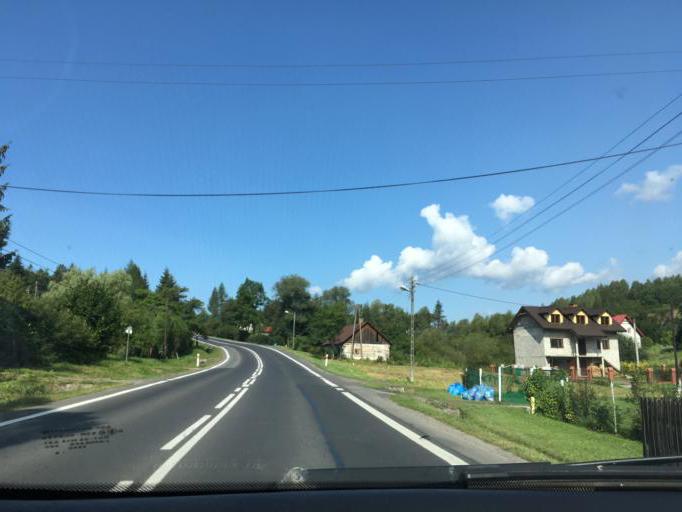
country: PL
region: Subcarpathian Voivodeship
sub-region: Powiat leski
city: Uherce Mineralne
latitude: 49.4653
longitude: 22.3937
